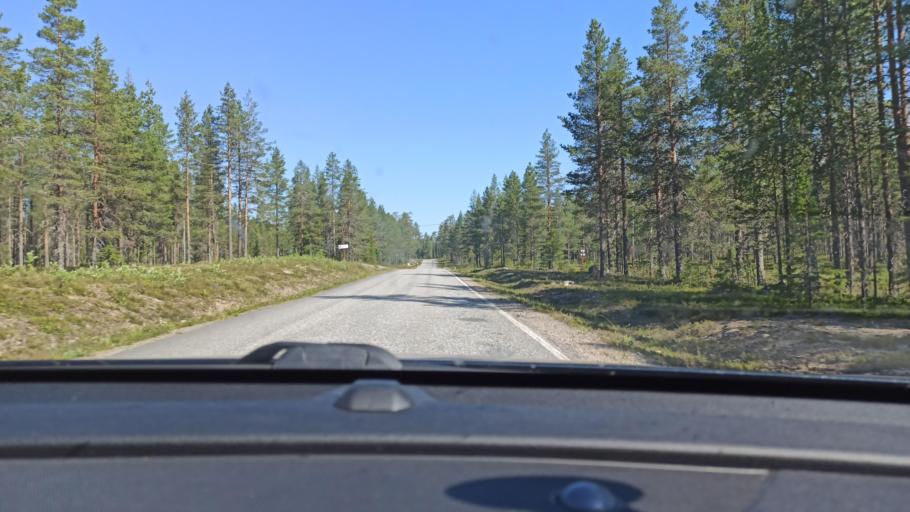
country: FI
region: Lapland
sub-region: Tunturi-Lappi
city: Kolari
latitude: 67.6561
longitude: 24.1643
